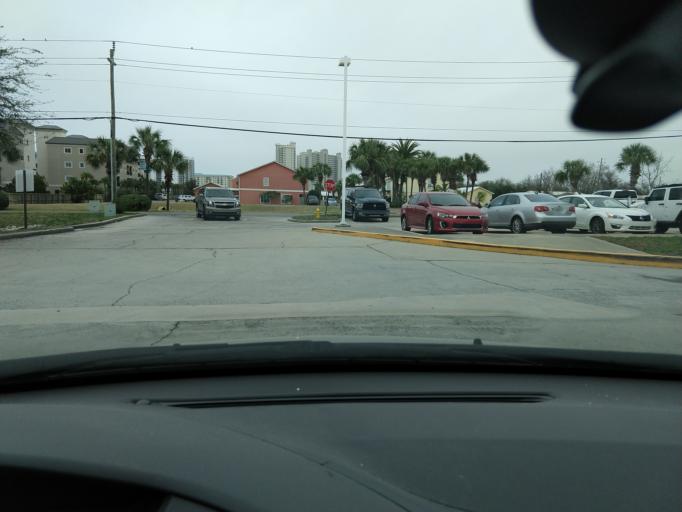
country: US
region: Florida
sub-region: Walton County
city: Miramar Beach
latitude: 30.3771
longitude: -86.3593
